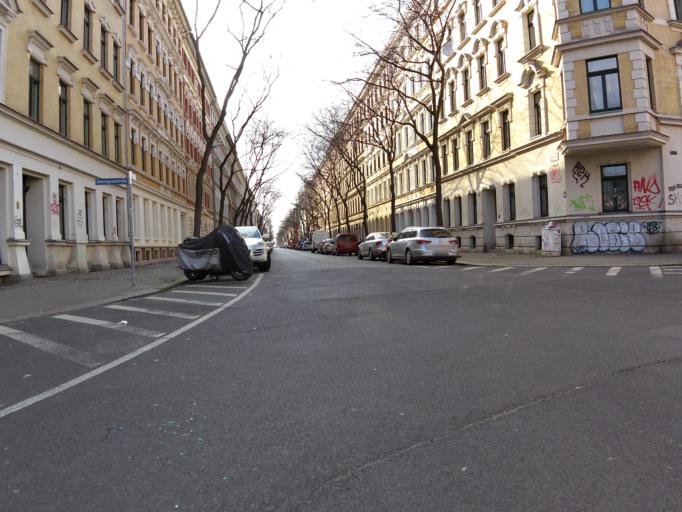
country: DE
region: Saxony
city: Leipzig
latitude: 51.3458
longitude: 12.4140
